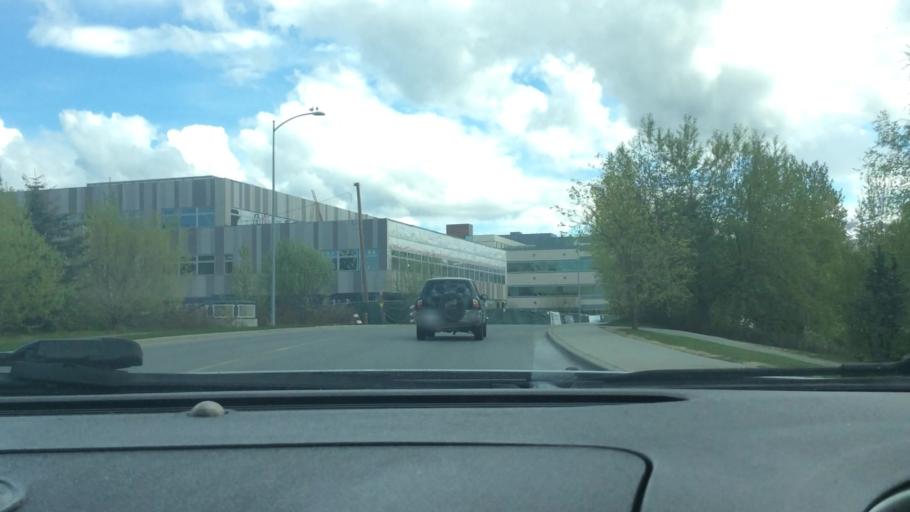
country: US
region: Alaska
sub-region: Anchorage Municipality
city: Anchorage
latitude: 61.1835
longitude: -149.8059
